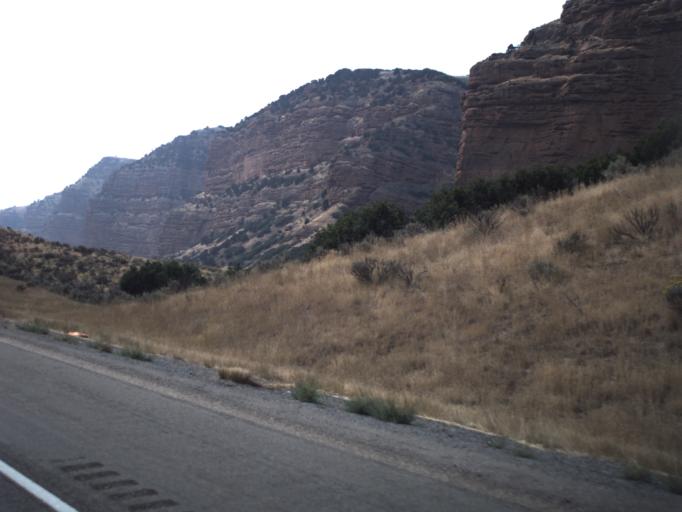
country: US
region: Utah
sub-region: Summit County
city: Coalville
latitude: 40.9964
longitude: -111.3965
